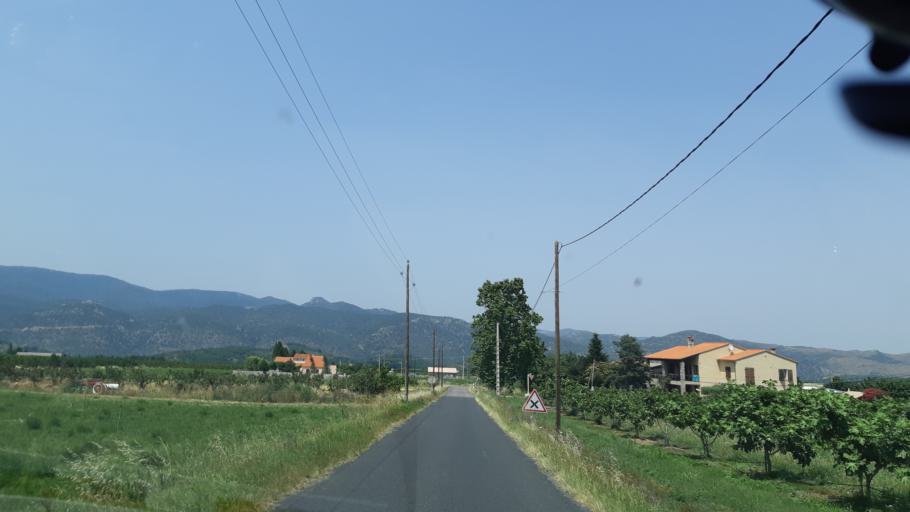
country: FR
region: Languedoc-Roussillon
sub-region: Departement des Pyrenees-Orientales
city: Vinca
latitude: 42.6197
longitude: 2.5188
